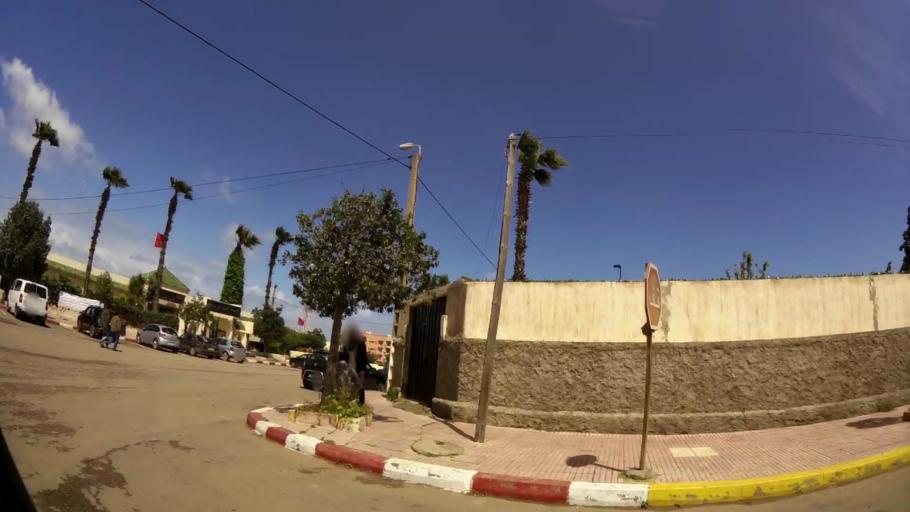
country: MA
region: Grand Casablanca
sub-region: Mediouna
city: Tit Mellil
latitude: 33.6358
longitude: -7.4549
